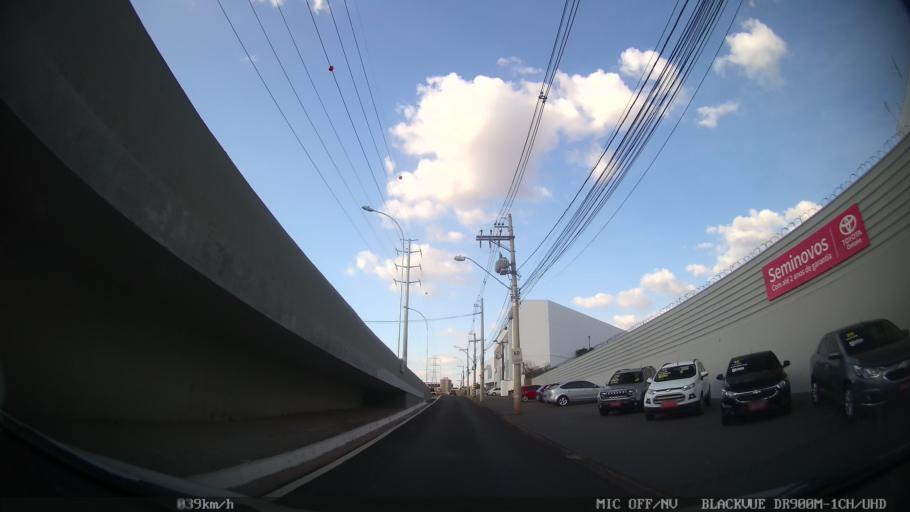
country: BR
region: Sao Paulo
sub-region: Ribeirao Preto
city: Ribeirao Preto
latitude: -21.1918
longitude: -47.7970
